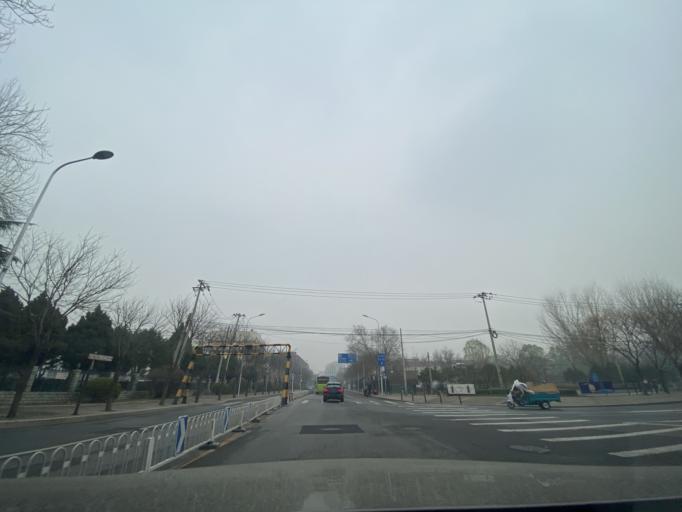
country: CN
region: Beijing
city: Sijiqing
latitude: 39.9652
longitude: 116.2686
